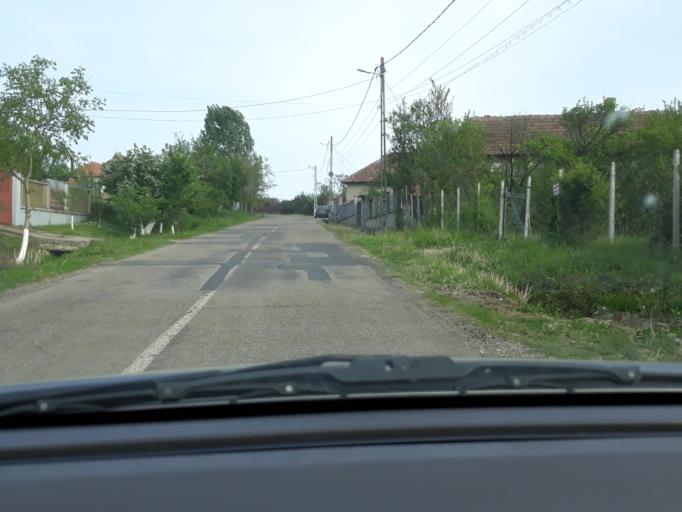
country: RO
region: Bihor
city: Hidiselu de Sus
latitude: 46.9741
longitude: 22.0113
